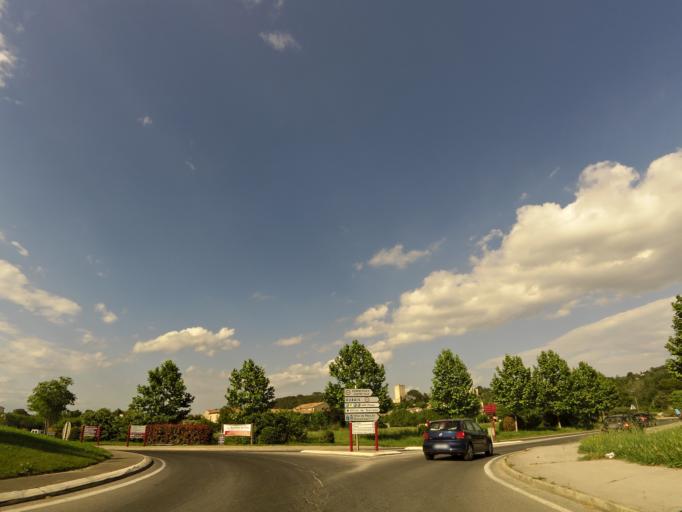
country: FR
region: Languedoc-Roussillon
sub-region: Departement du Gard
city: Sommieres
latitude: 43.7788
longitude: 4.0866
